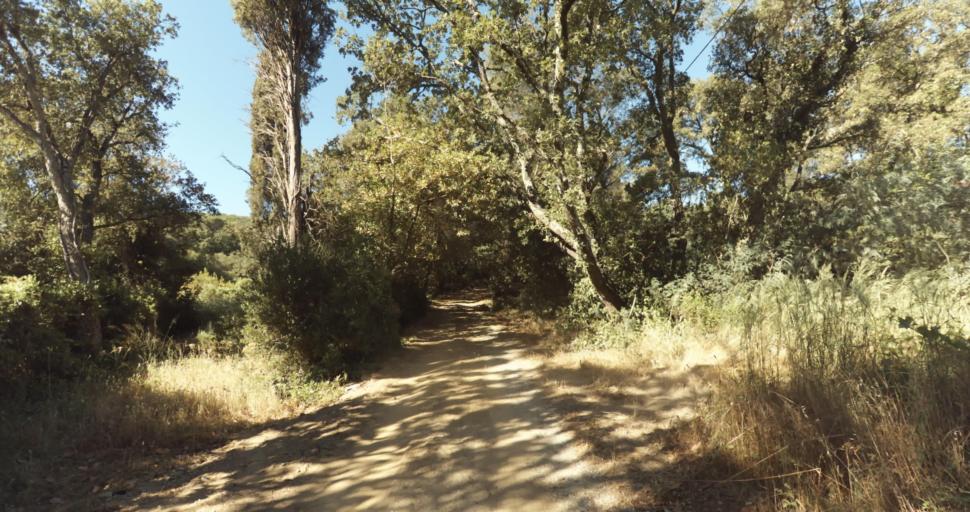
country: FR
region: Provence-Alpes-Cote d'Azur
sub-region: Departement du Var
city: Saint-Tropez
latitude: 43.2587
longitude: 6.6171
